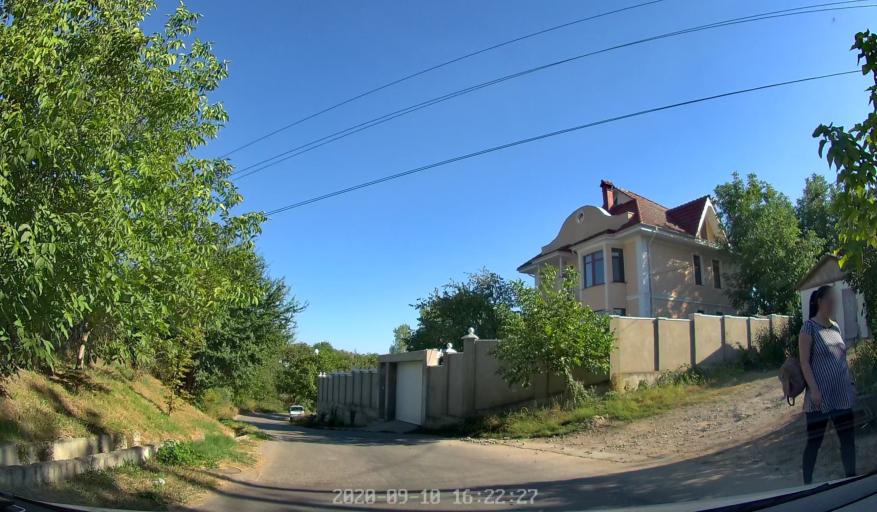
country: MD
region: Chisinau
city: Stauceni
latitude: 47.0530
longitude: 28.9247
